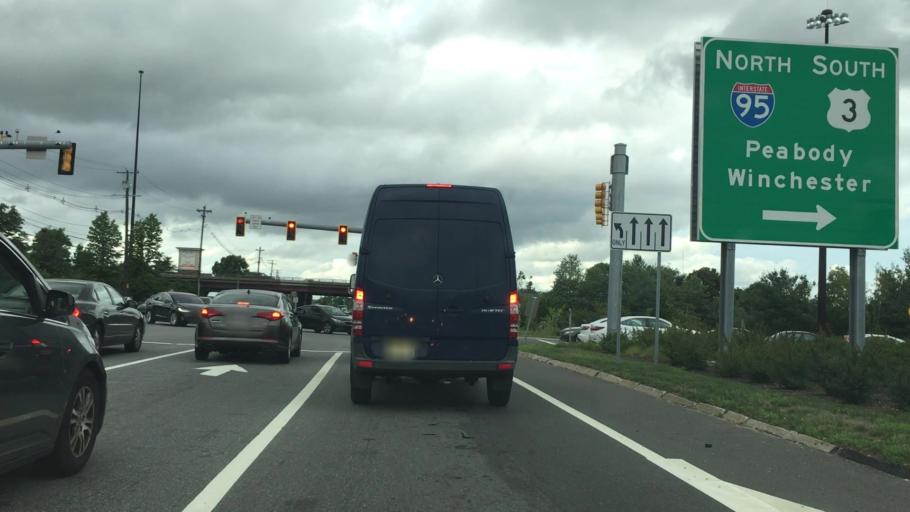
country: US
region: Massachusetts
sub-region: Middlesex County
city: Lexington
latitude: 42.4763
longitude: -71.2141
